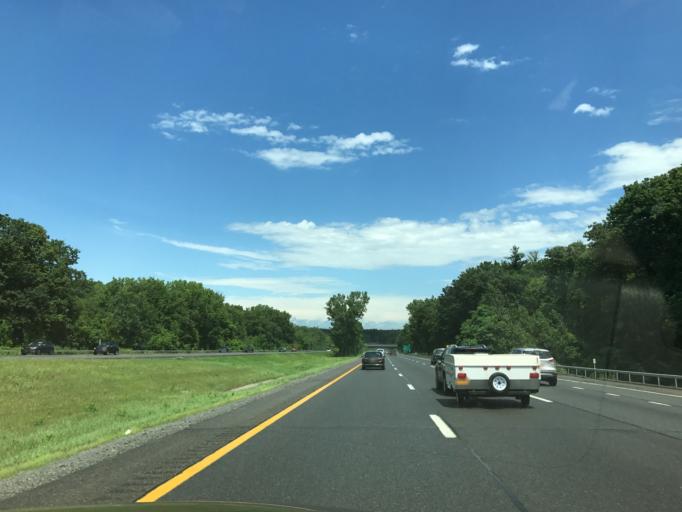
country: US
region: New York
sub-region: Saratoga County
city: Country Knolls
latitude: 42.8824
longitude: -73.7782
